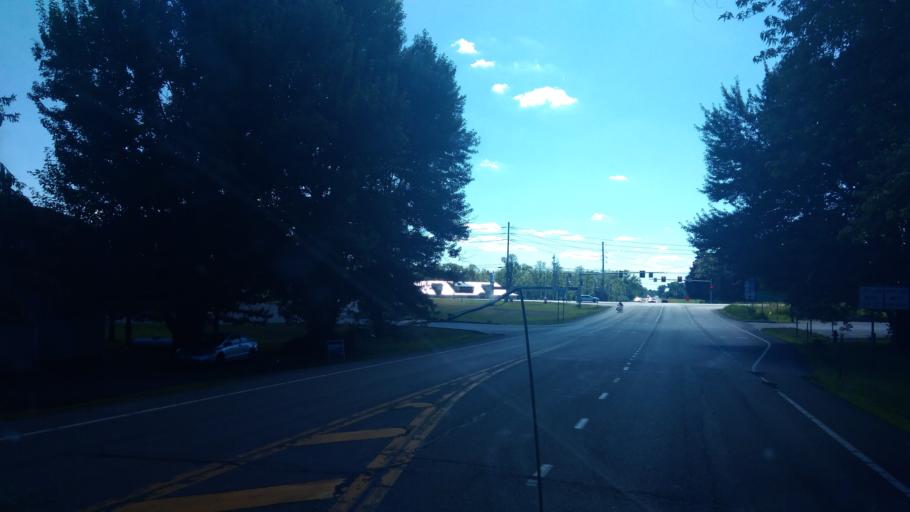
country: US
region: New York
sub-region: Seneca County
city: Waterloo
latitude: 42.9612
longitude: -76.8444
